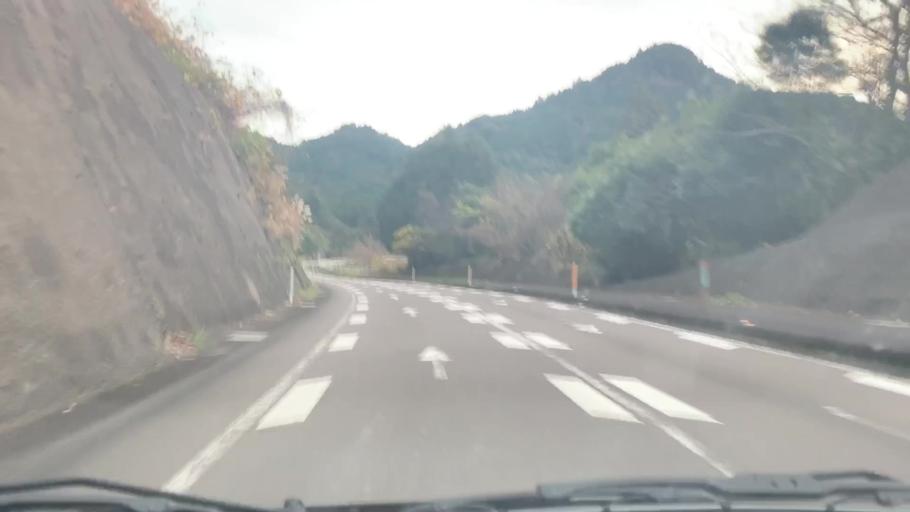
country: JP
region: Saga Prefecture
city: Kashima
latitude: 33.0514
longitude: 130.0729
